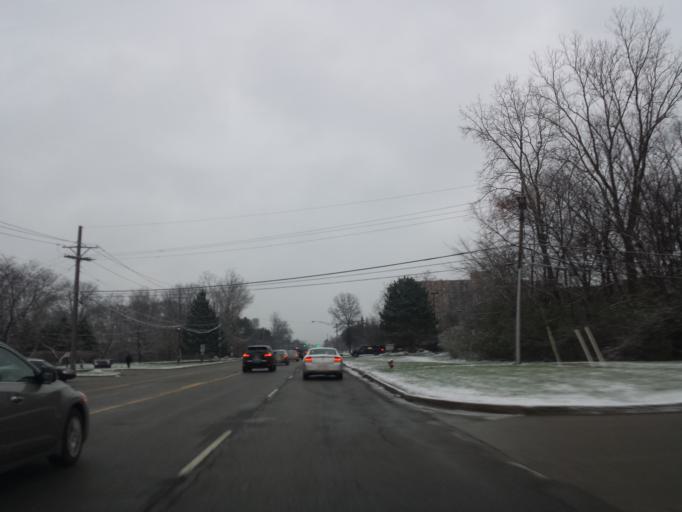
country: US
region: Michigan
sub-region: Oakland County
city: Franklin
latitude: 42.5006
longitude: -83.3031
